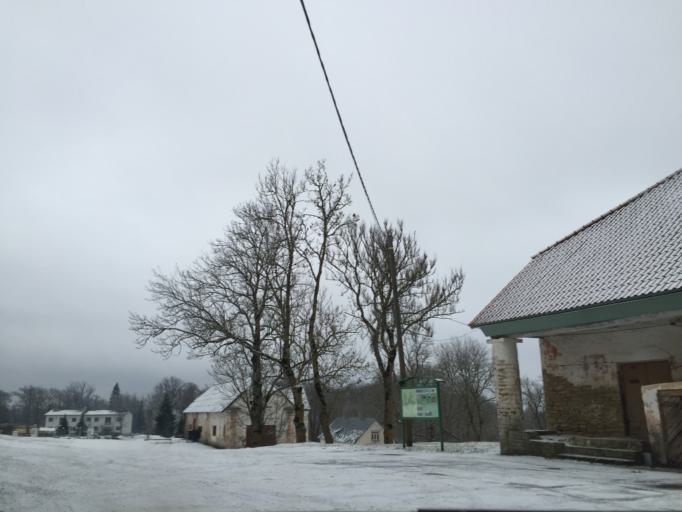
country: EE
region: Laeaene
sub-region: Lihula vald
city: Lihula
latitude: 58.6934
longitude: 23.8381
